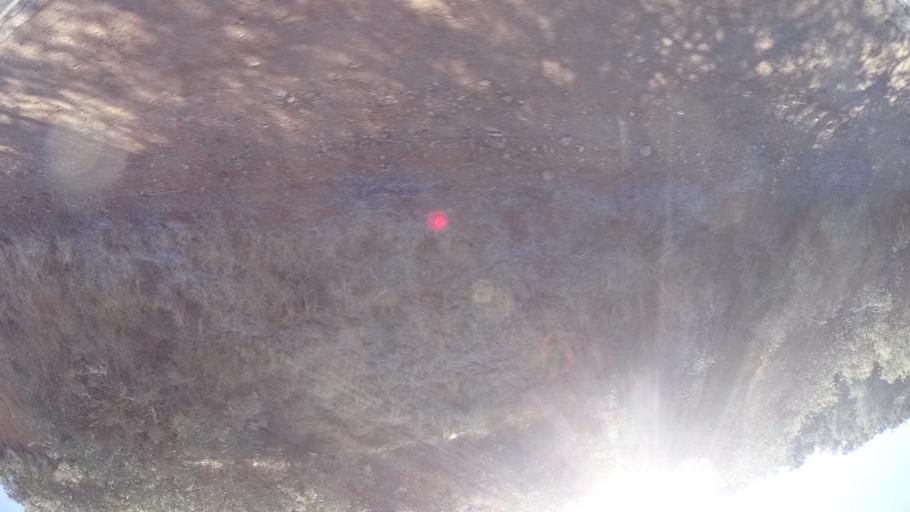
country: US
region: California
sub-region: Kern County
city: Maricopa
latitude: 34.8792
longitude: -119.3486
